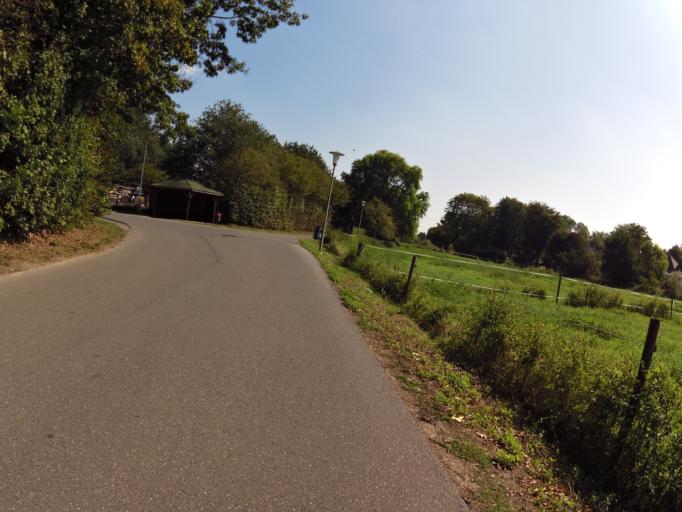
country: DE
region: North Rhine-Westphalia
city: Stadtlohn
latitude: 51.9978
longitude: 6.9298
